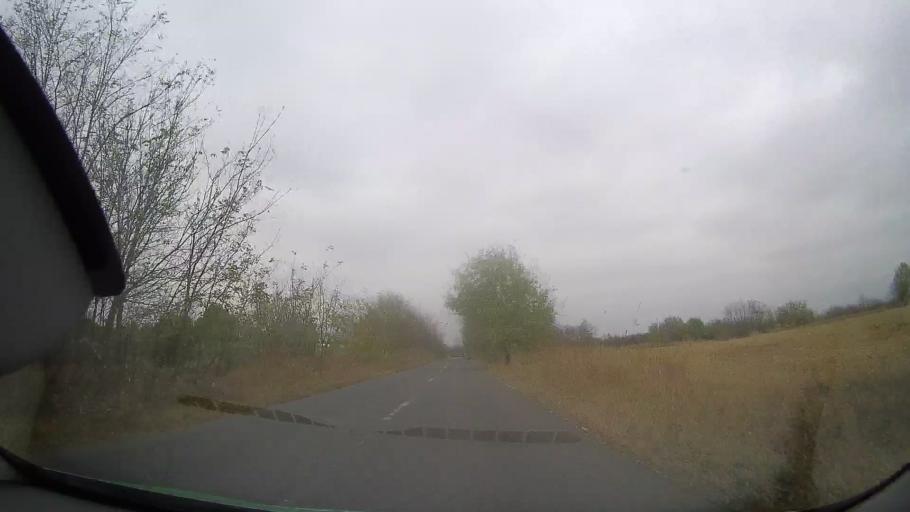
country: RO
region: Buzau
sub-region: Comuna Bradeanu
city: Bradeanu
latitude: 44.9191
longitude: 26.8678
